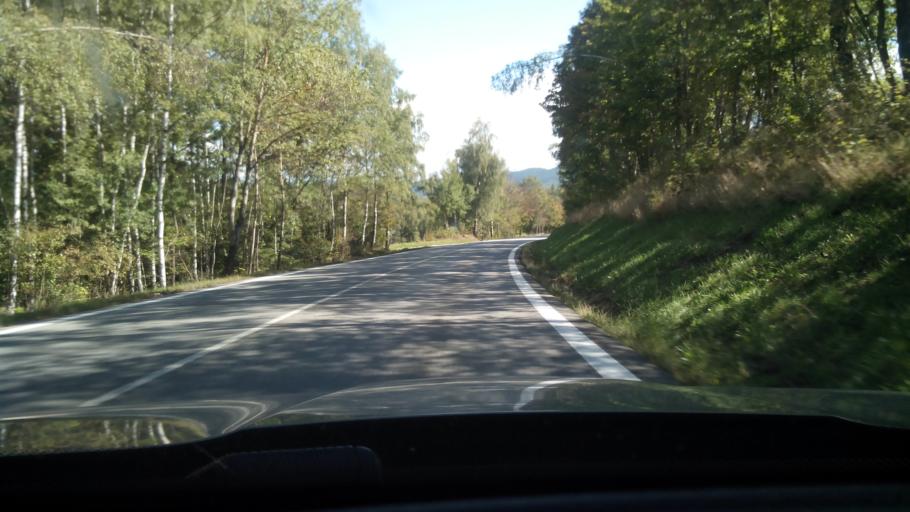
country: CZ
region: Jihocesky
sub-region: Okres Prachatice
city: Vimperk
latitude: 49.0634
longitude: 13.7501
